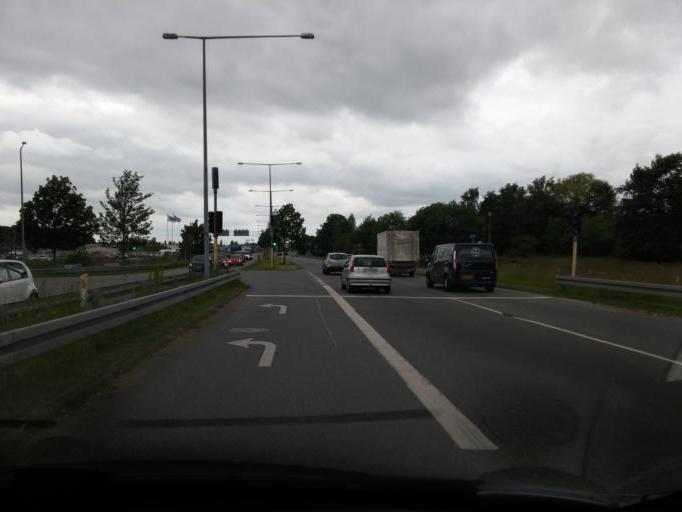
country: DK
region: Capital Region
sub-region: Hillerod Kommune
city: Hillerod
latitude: 55.9311
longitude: 12.2926
